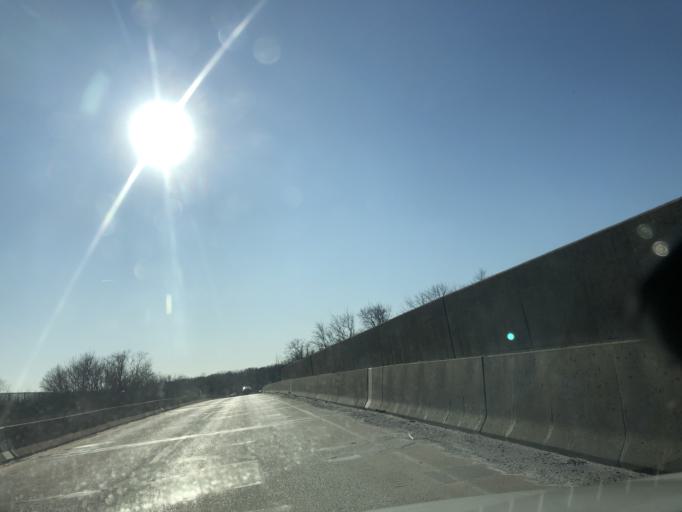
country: US
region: Pennsylvania
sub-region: Bucks County
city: Morrisville
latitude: 40.1946
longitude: -74.8016
